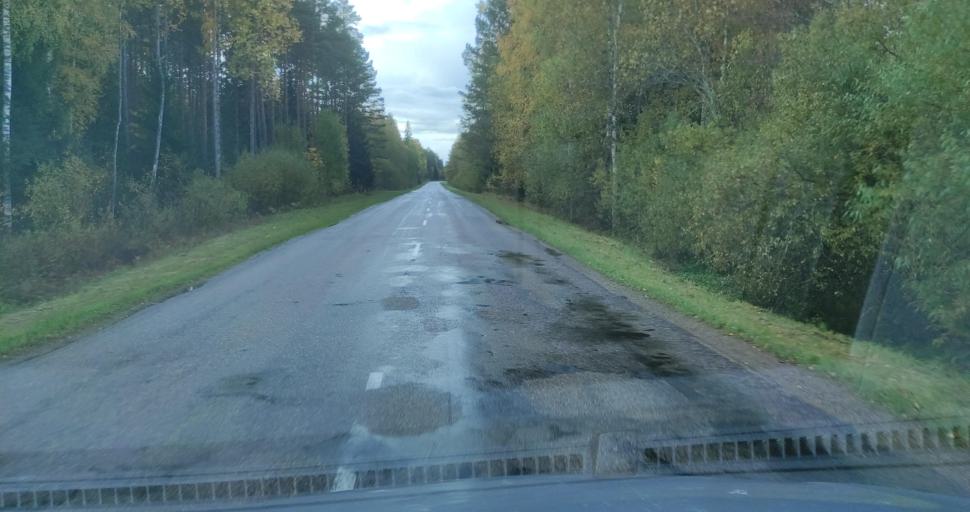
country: LV
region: Skrunda
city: Skrunda
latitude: 56.6589
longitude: 22.0213
